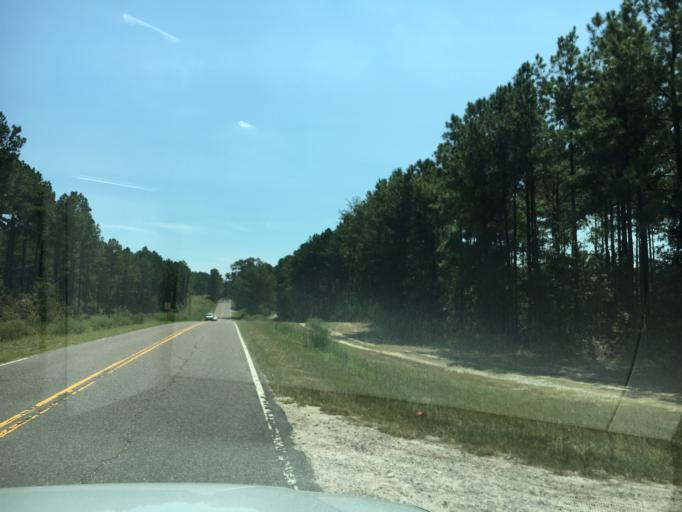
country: US
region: South Carolina
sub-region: Lexington County
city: Batesburg
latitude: 33.8170
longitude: -81.6543
